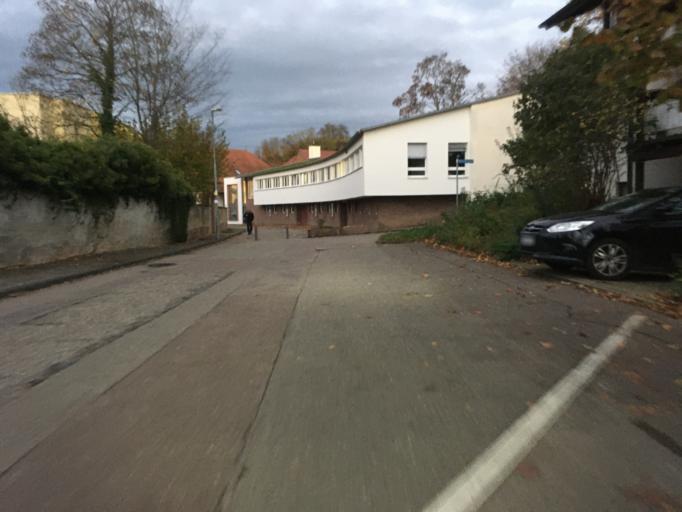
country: DE
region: Baden-Wuerttemberg
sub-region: Freiburg Region
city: Riegel
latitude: 48.1493
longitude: 7.7480
